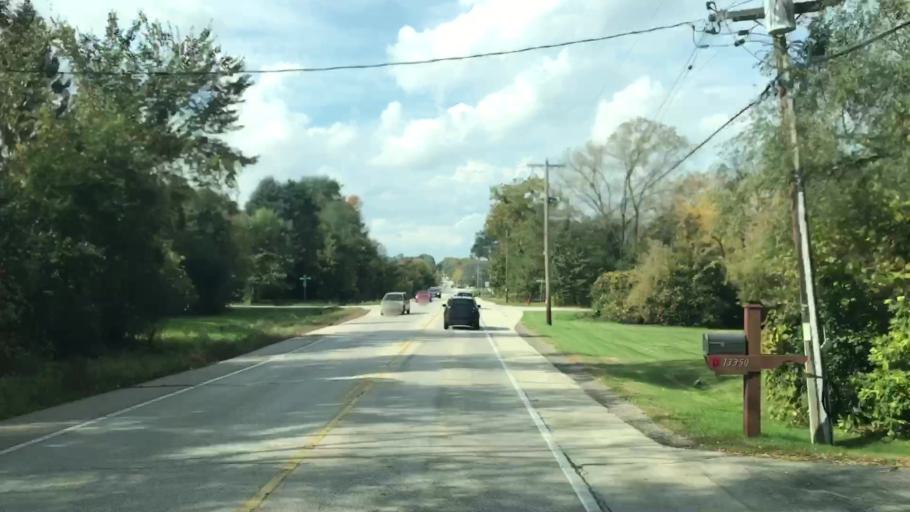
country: US
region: Wisconsin
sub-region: Waukesha County
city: Elm Grove
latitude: 43.0603
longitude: -88.0789
